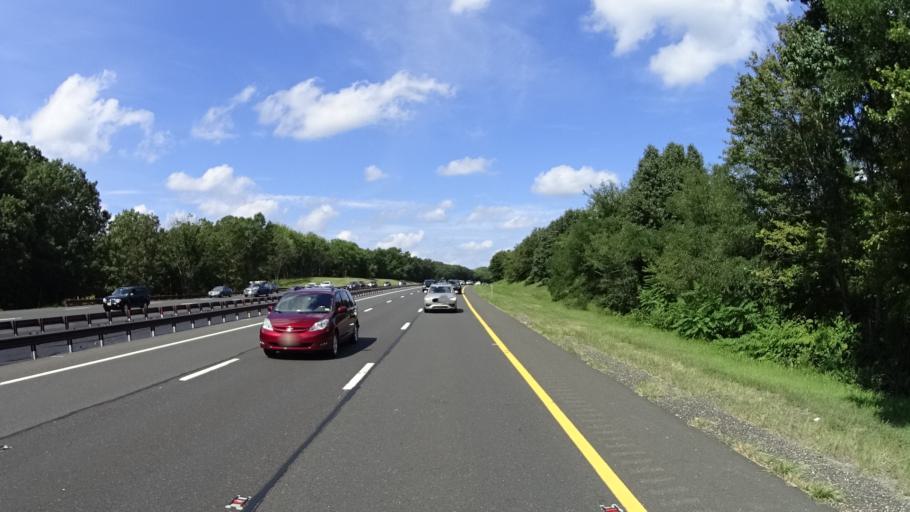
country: US
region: New Jersey
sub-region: Monmouth County
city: Matawan
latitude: 40.4289
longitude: -74.2373
